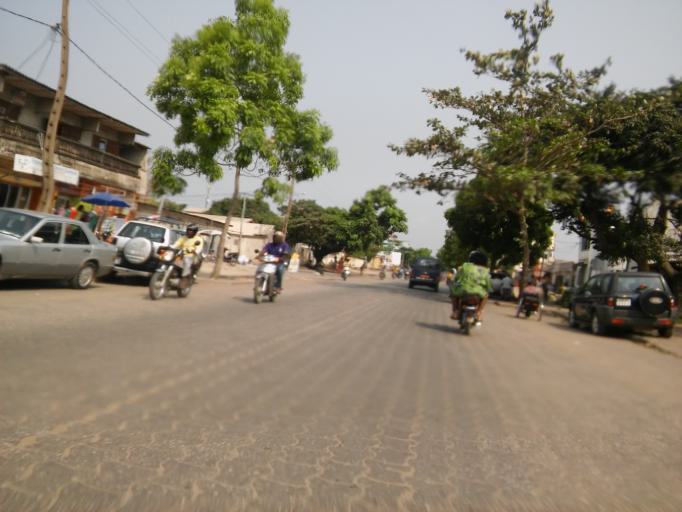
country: BJ
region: Littoral
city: Cotonou
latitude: 6.3909
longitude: 2.3937
